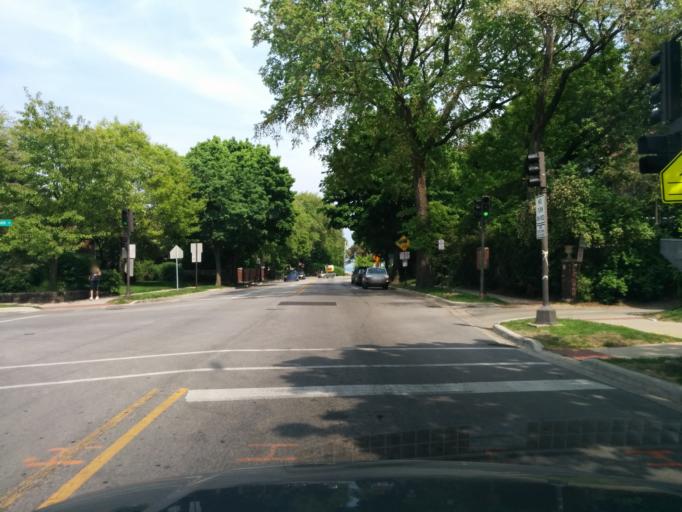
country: US
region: Illinois
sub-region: Cook County
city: Evanston
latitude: 42.0339
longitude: -87.6723
